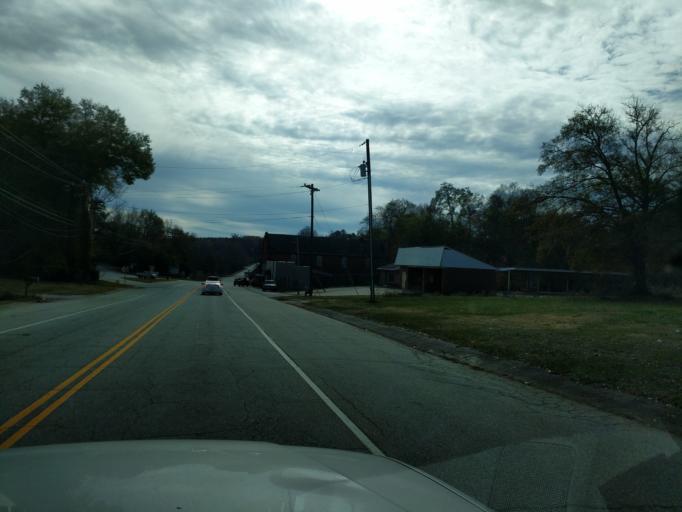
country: US
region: South Carolina
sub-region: Spartanburg County
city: Woodruff
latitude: 34.6548
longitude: -81.9650
